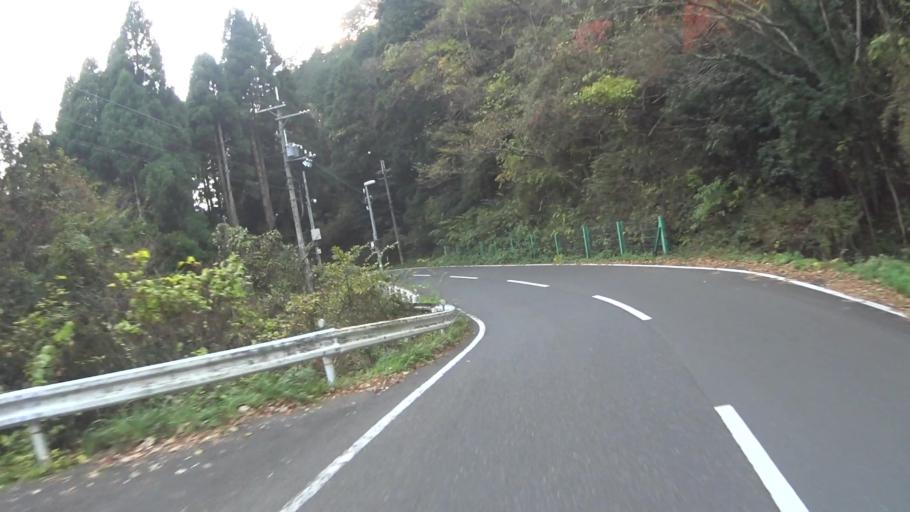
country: JP
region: Kyoto
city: Maizuru
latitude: 35.5389
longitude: 135.4478
